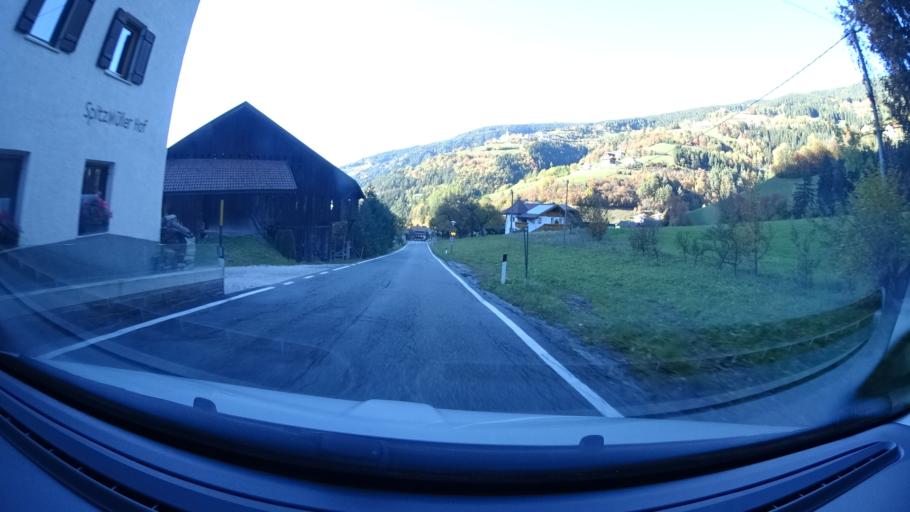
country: IT
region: Trentino-Alto Adige
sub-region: Bolzano
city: Ortisei
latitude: 46.5928
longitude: 11.6203
